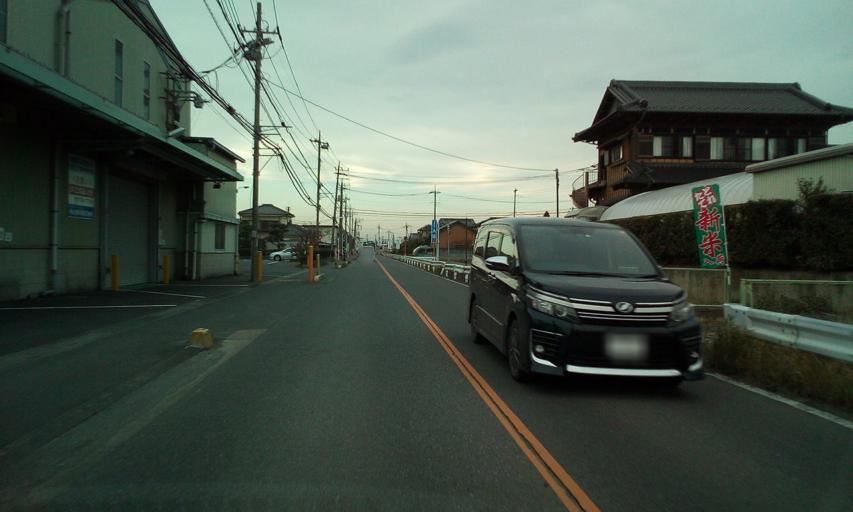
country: JP
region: Saitama
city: Yashio-shi
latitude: 35.8451
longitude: 139.8629
